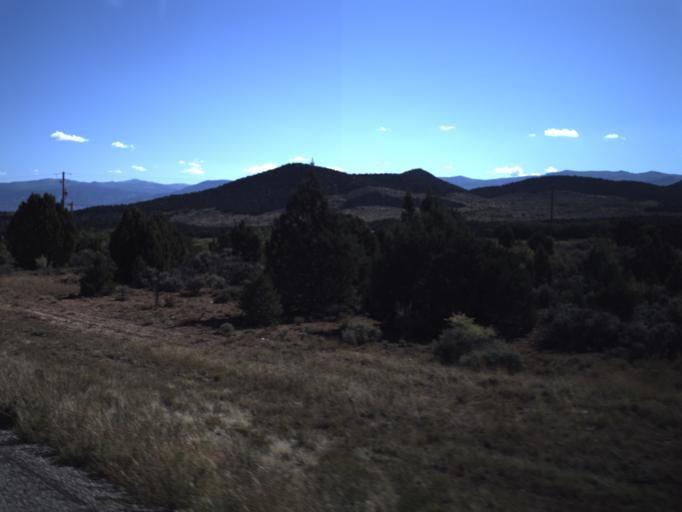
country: US
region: Utah
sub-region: Iron County
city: Cedar City
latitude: 37.6272
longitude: -113.3137
